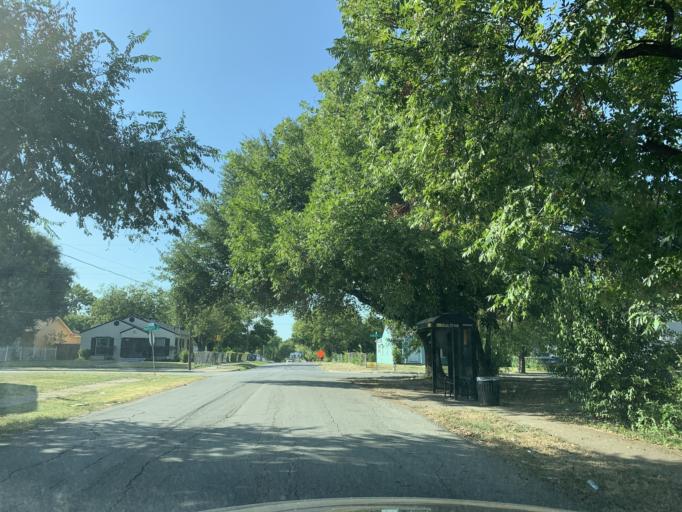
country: US
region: Texas
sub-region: Dallas County
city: Dallas
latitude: 32.7063
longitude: -96.7897
